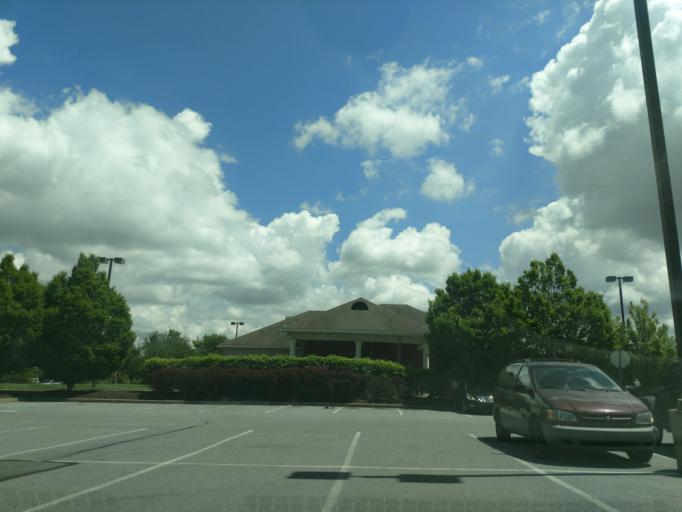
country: US
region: Pennsylvania
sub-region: Chester County
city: Exton
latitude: 40.0562
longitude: -75.6664
